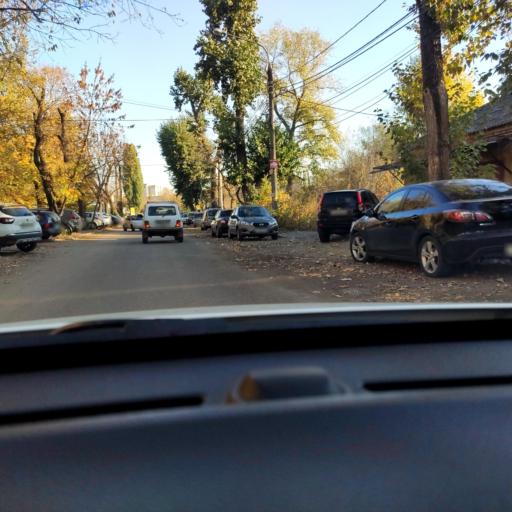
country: RU
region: Voronezj
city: Voronezh
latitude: 51.6771
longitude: 39.1729
